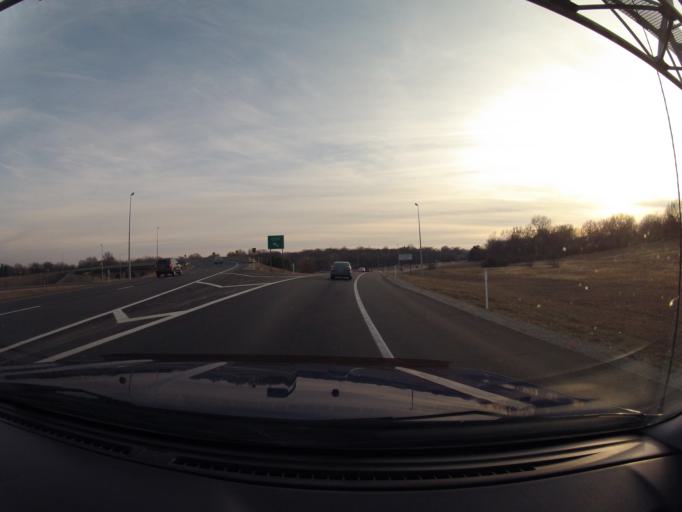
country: US
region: Kansas
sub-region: Shawnee County
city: Topeka
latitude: 39.0683
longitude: -95.7320
